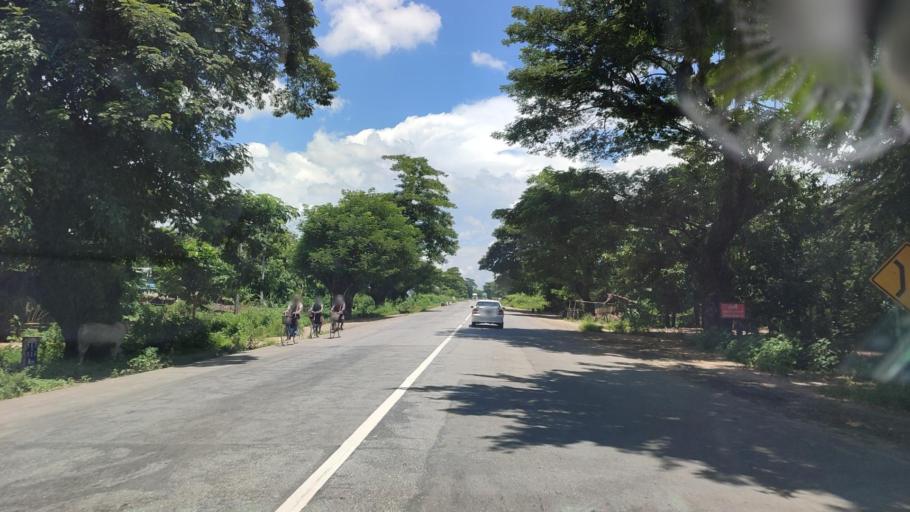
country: MM
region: Bago
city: Nyaunglebin
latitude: 18.1822
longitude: 96.5944
